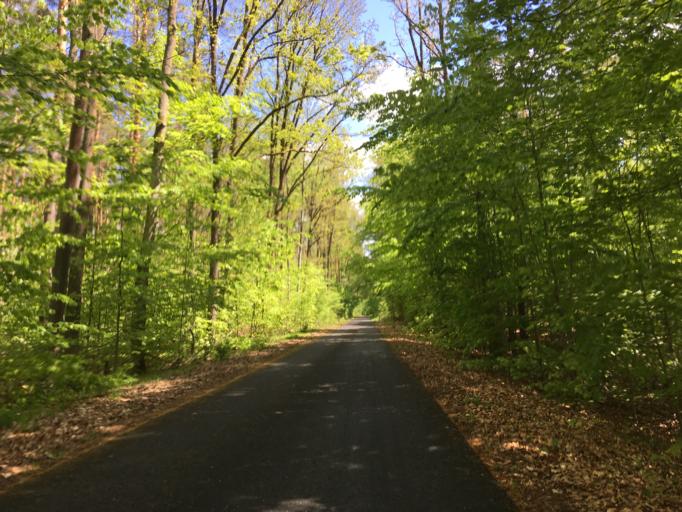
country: DE
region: Brandenburg
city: Oranienburg
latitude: 52.8058
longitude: 13.3225
